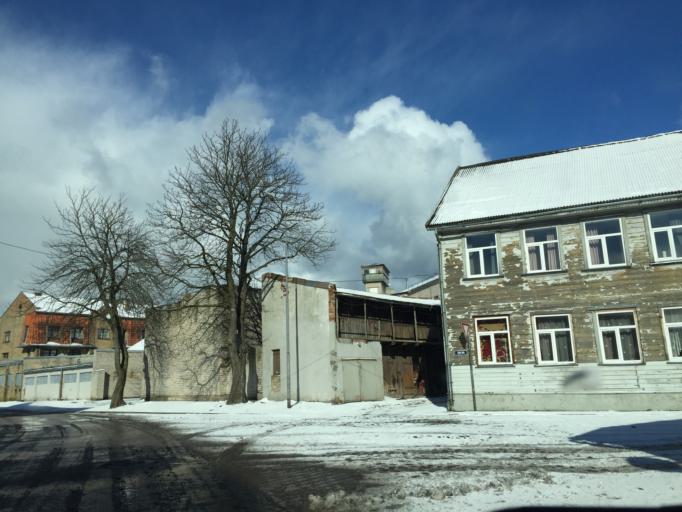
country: LV
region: Ventspils
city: Ventspils
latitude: 57.3947
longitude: 21.5612
